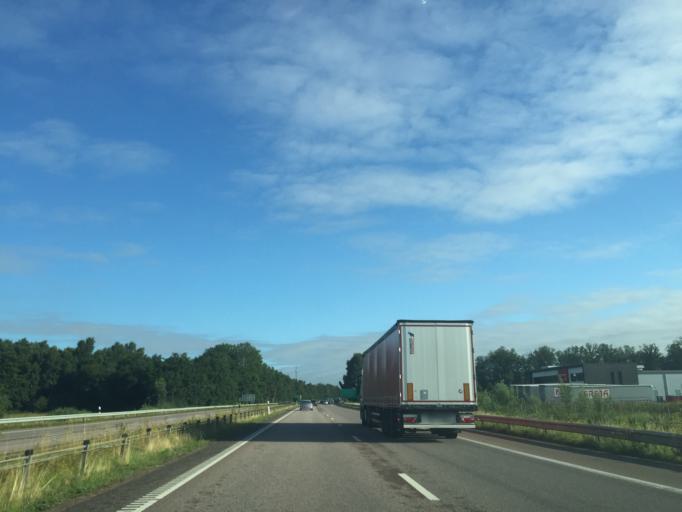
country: SE
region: Skane
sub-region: Helsingborg
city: Odakra
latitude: 56.0698
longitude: 12.7797
